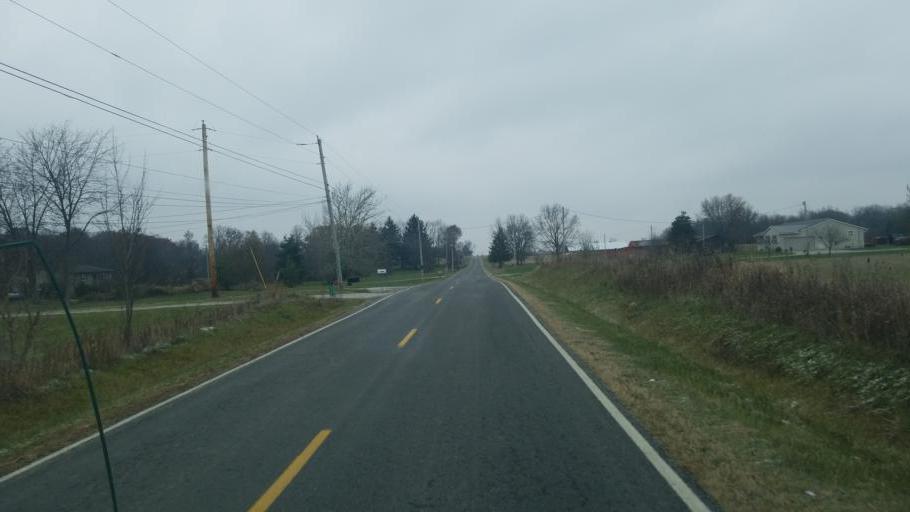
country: US
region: Ohio
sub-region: Medina County
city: Lodi
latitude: 41.1272
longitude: -82.0021
